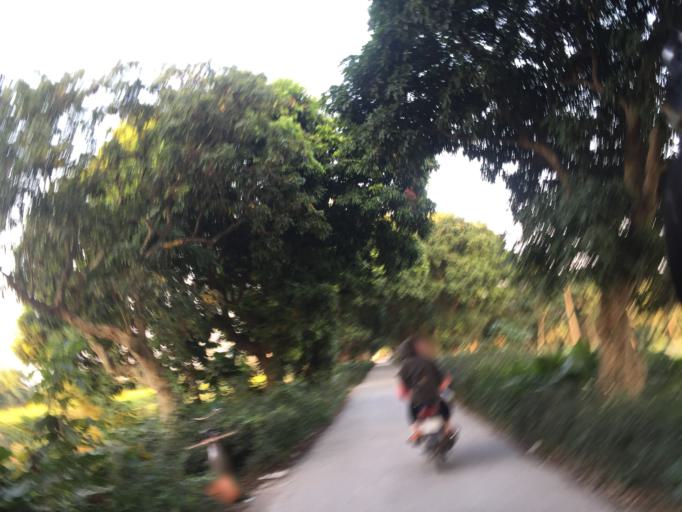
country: VN
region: Ha Noi
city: Chuc Son
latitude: 20.9071
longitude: 105.7260
